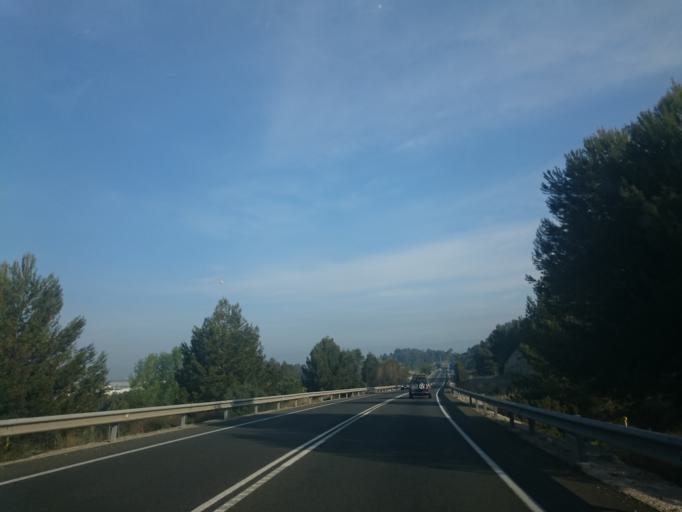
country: ES
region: Catalonia
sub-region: Provincia de Barcelona
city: La Pobla de Claramunt
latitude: 41.5671
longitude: 1.6760
